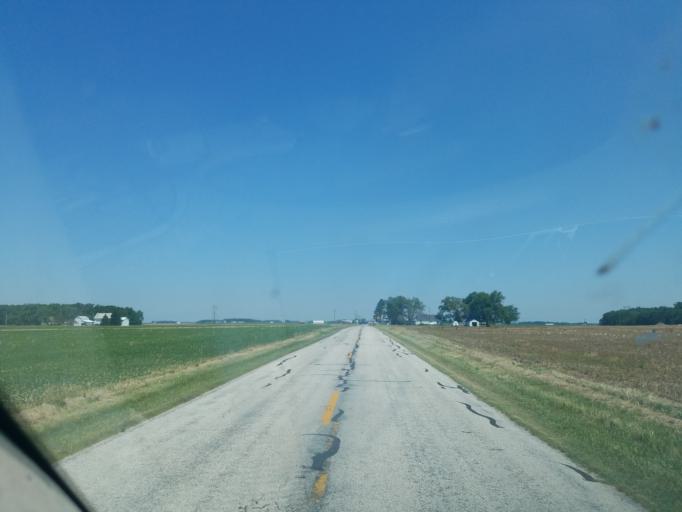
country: US
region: Ohio
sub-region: Mercer County
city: Rockford
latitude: 40.6082
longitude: -84.7085
